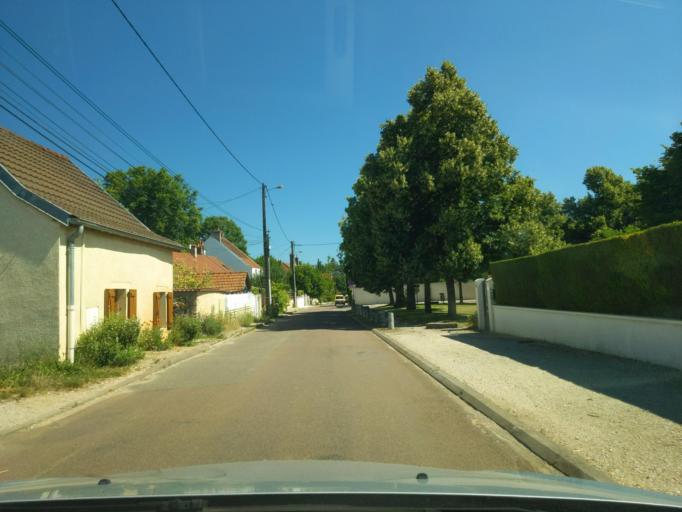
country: FR
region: Bourgogne
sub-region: Departement de la Cote-d'Or
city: Ruffey-les-Echirey
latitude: 47.3996
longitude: 5.0858
